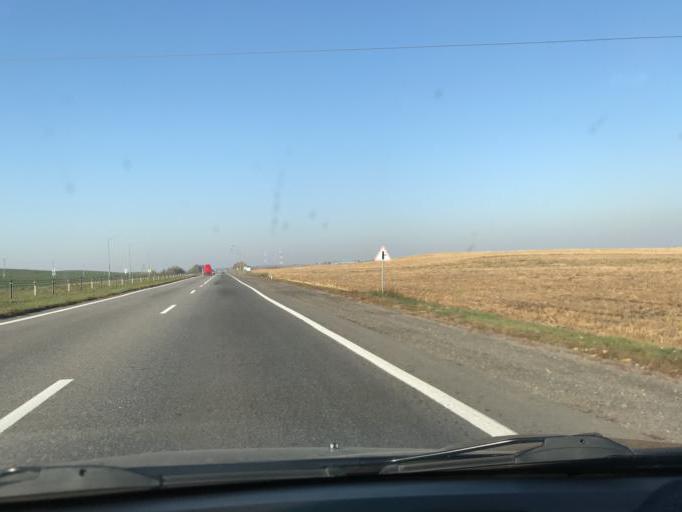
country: BY
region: Minsk
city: Luhavaya Slabada
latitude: 53.7215
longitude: 27.8620
